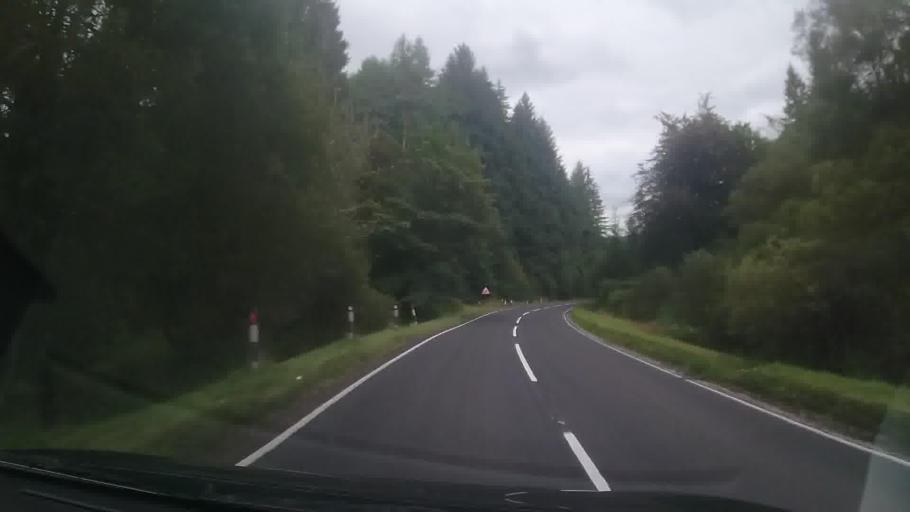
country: GB
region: Scotland
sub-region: Argyll and Bute
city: Garelochhead
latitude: 56.2505
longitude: -5.0912
